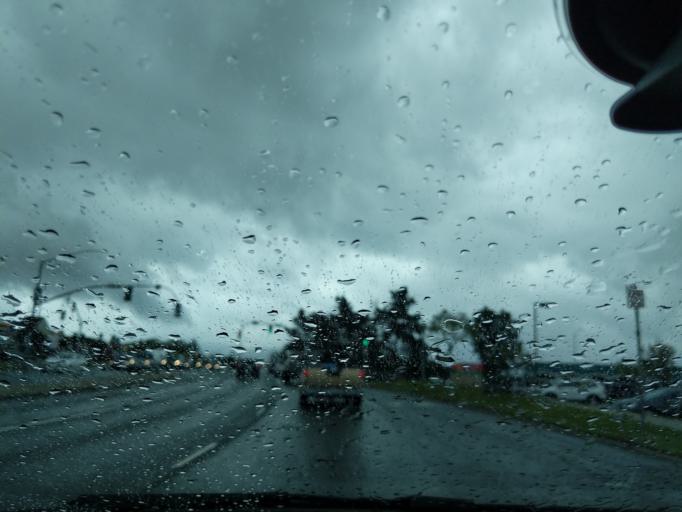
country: US
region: California
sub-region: Monterey County
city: Boronda
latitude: 36.6968
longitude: -121.6689
